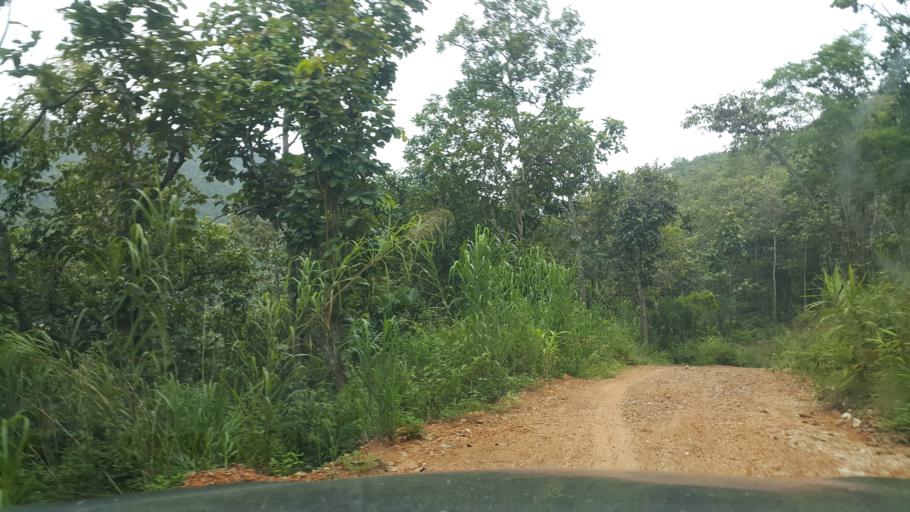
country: TH
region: Chiang Mai
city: San Sai
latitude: 18.9580
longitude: 99.1311
